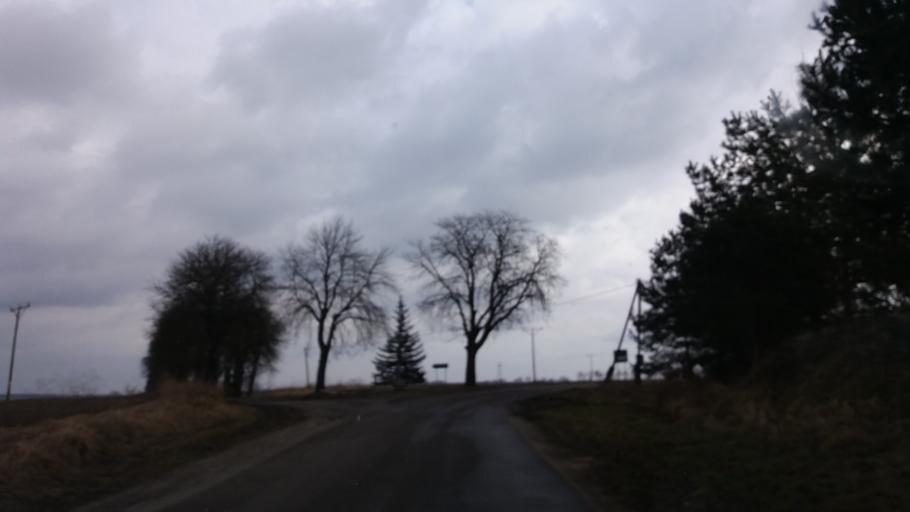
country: PL
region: West Pomeranian Voivodeship
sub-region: Powiat choszczenski
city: Recz
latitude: 53.2527
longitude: 15.5906
